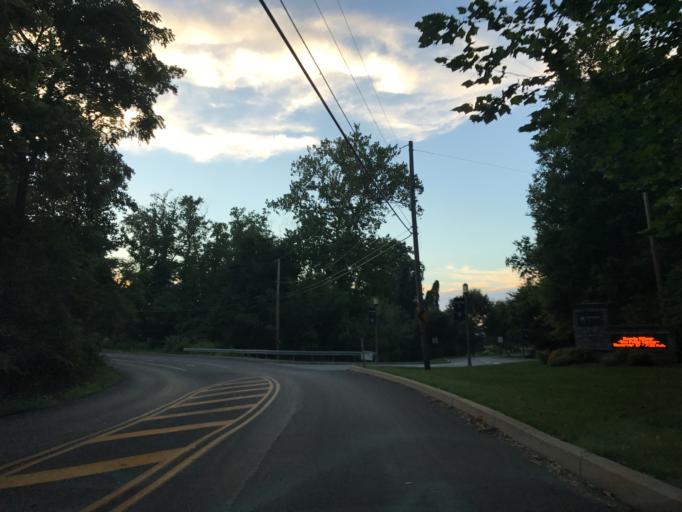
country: US
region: Pennsylvania
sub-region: York County
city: Valley View
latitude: 39.9492
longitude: -76.7047
